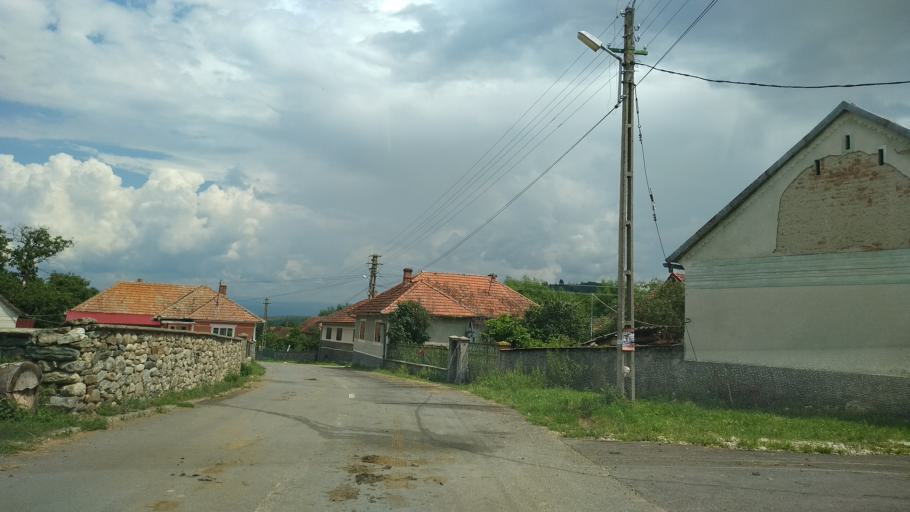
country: RO
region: Hunedoara
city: Salasu de Sus
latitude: 45.4785
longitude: 22.9117
